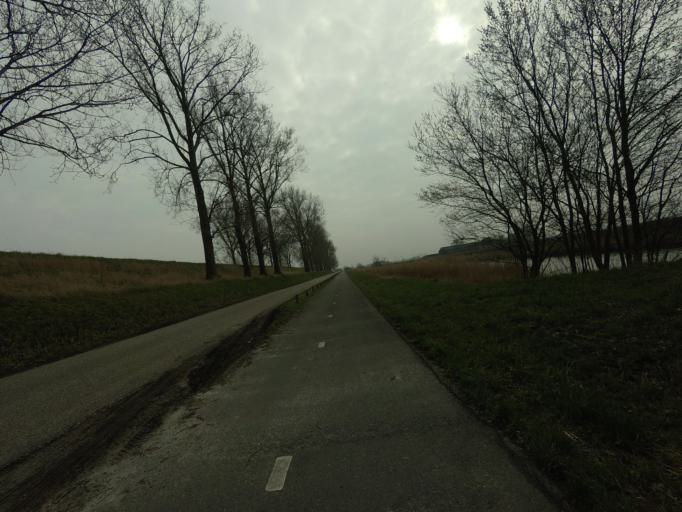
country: NL
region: Zeeland
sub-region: Gemeente Hulst
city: Hulst
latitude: 51.3502
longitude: 4.1085
